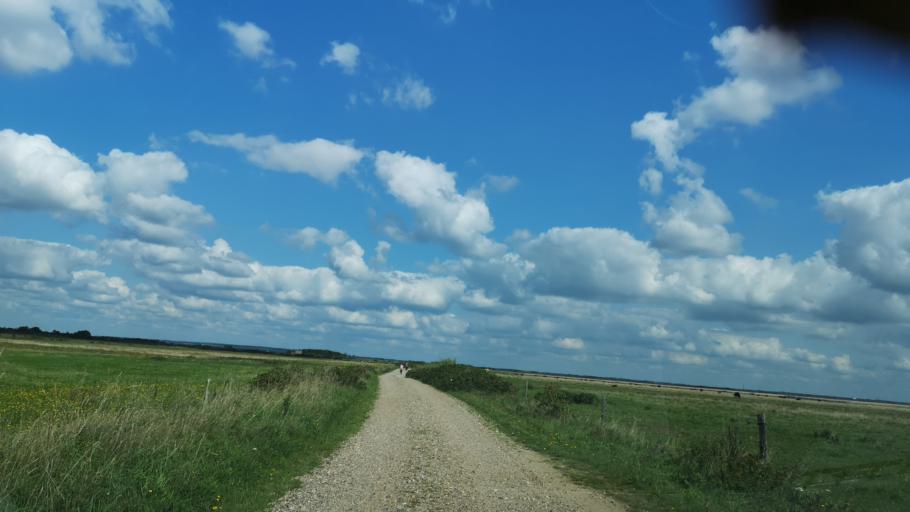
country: DK
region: Central Jutland
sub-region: Ringkobing-Skjern Kommune
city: Skjern
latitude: 55.9097
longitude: 8.4010
